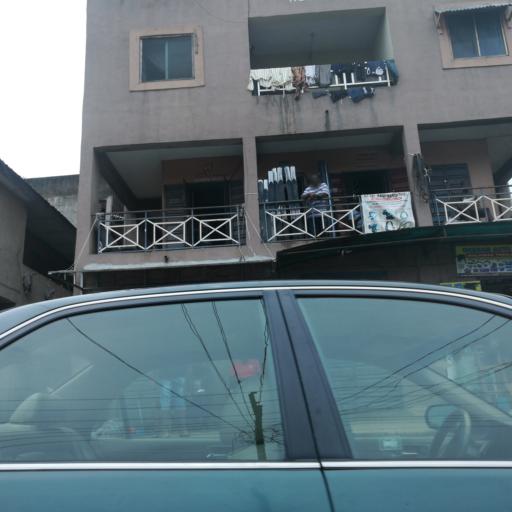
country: NG
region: Lagos
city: Ebute Metta
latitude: 6.4791
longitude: 3.3852
